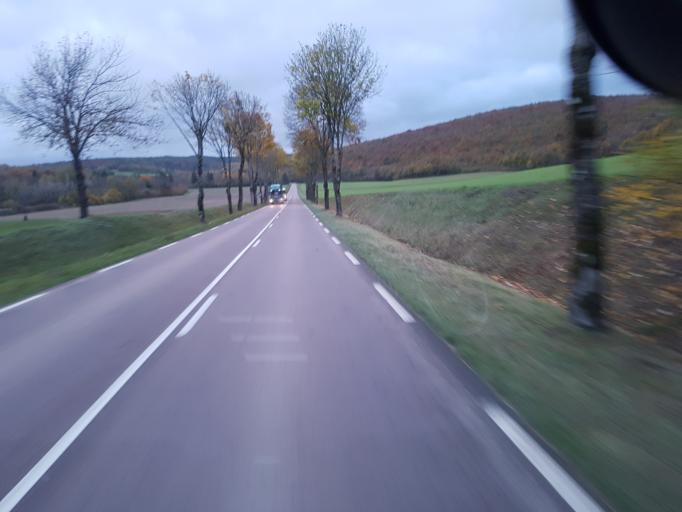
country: FR
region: Champagne-Ardenne
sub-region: Departement de l'Aube
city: Mussy-sur-Seine
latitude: 48.0025
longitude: 4.4744
